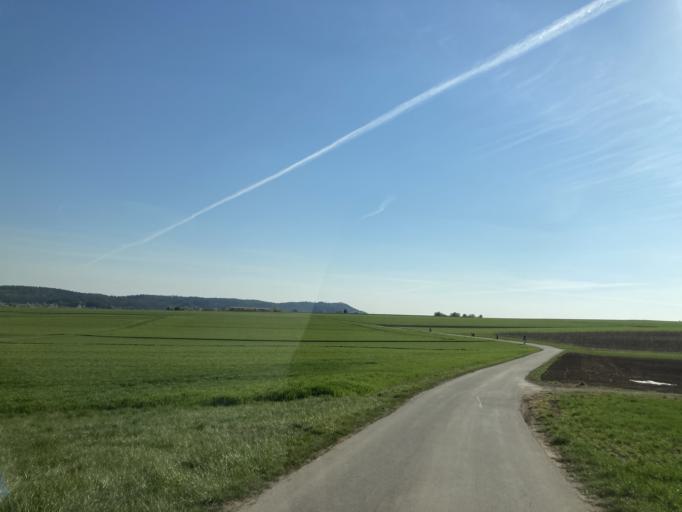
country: DE
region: Baden-Wuerttemberg
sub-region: Tuebingen Region
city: Rottenburg
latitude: 48.5470
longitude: 8.9583
